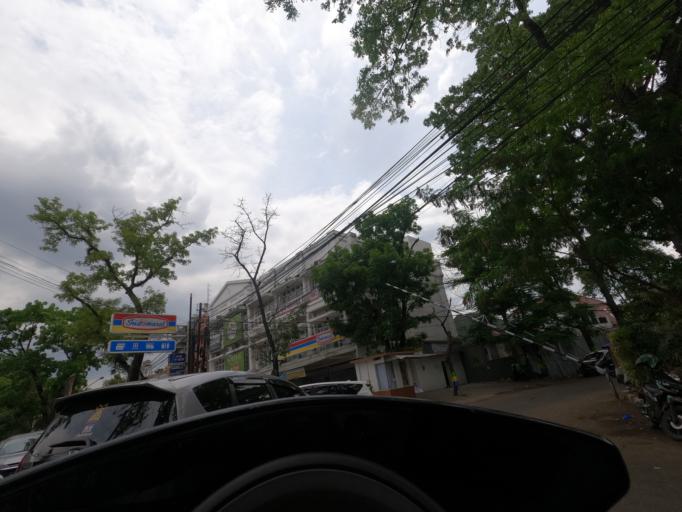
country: ID
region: West Java
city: Bandung
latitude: -6.9085
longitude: 107.6270
